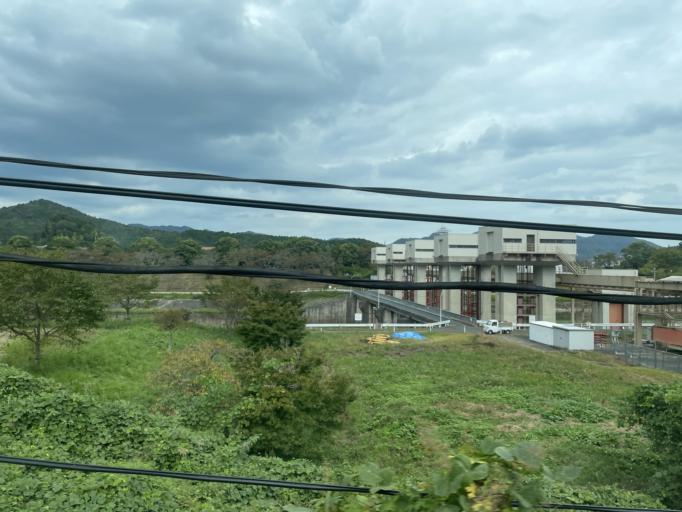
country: JP
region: Hyogo
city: Sasayama
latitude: 35.0795
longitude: 135.1588
